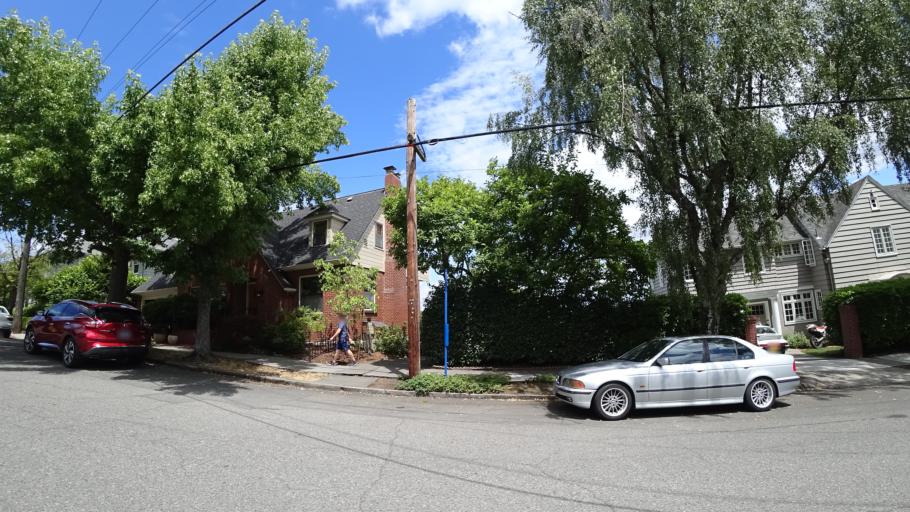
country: US
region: Oregon
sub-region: Multnomah County
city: Portland
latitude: 45.5302
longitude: -122.7093
